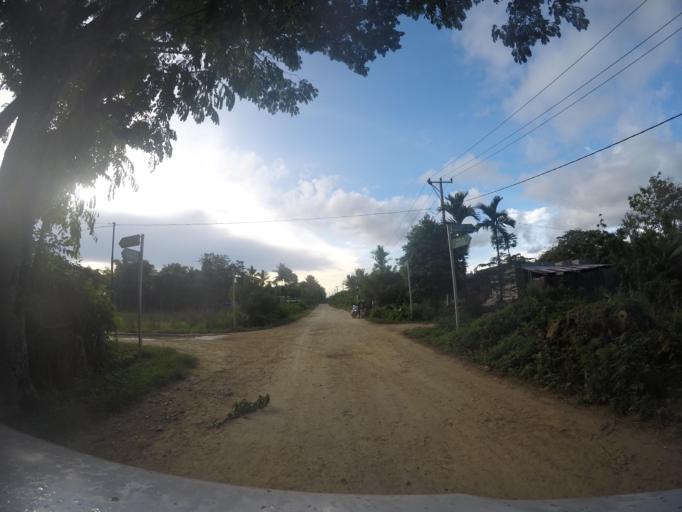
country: TL
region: Lautem
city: Lospalos
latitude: -8.4990
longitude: 126.9982
